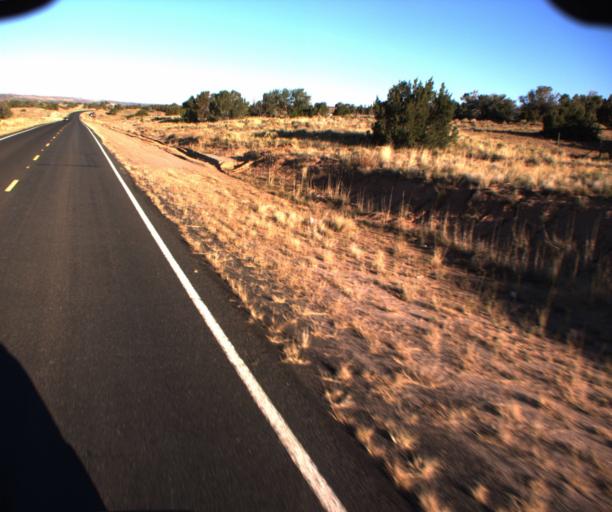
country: US
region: Arizona
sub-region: Apache County
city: Houck
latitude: 35.3754
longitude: -109.4870
